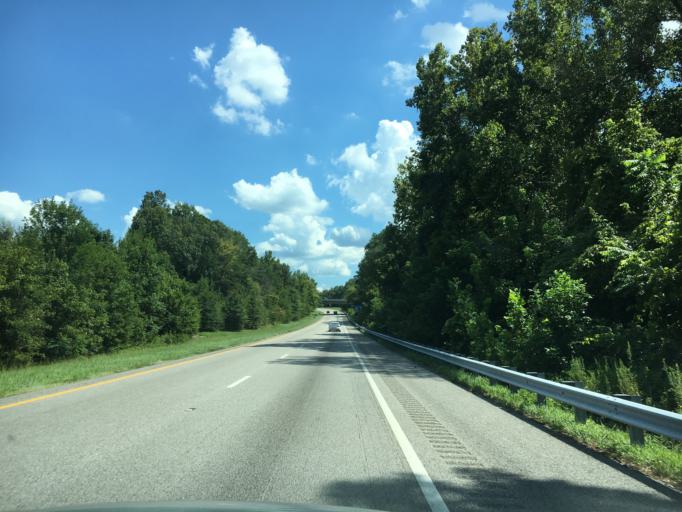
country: US
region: South Carolina
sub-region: Laurens County
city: Clinton
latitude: 34.5159
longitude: -81.8721
